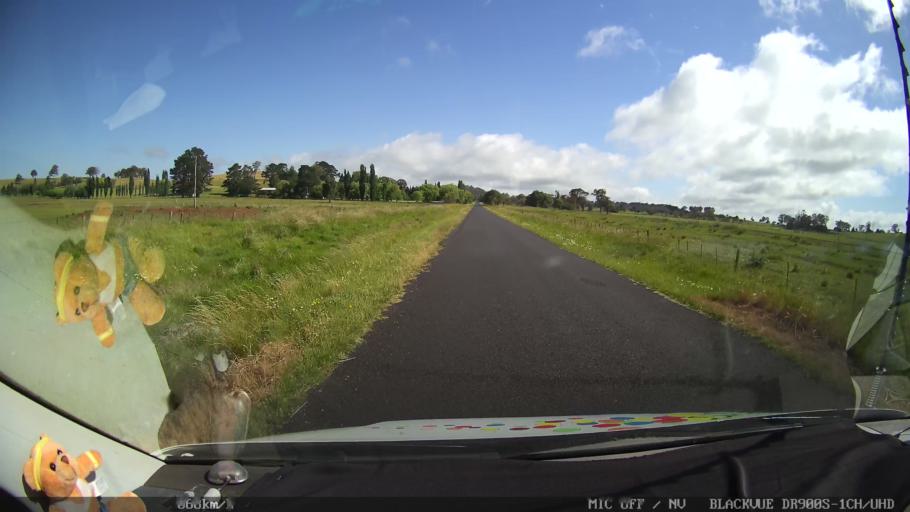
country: AU
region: New South Wales
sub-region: Guyra
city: Guyra
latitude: -30.0510
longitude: 151.6659
